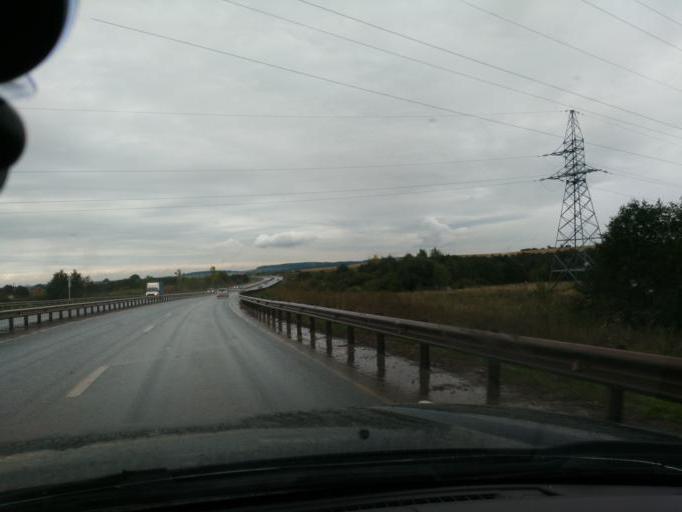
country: RU
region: Perm
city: Kultayevo
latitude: 57.8862
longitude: 55.9281
